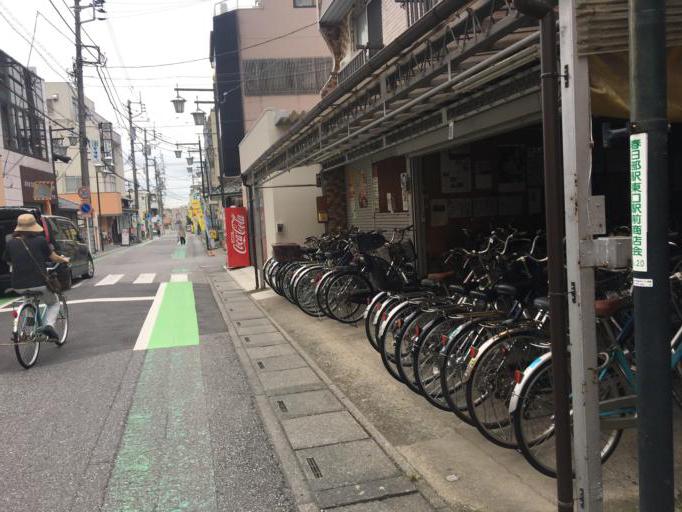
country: JP
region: Saitama
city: Kasukabe
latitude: 35.9809
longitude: 139.7521
